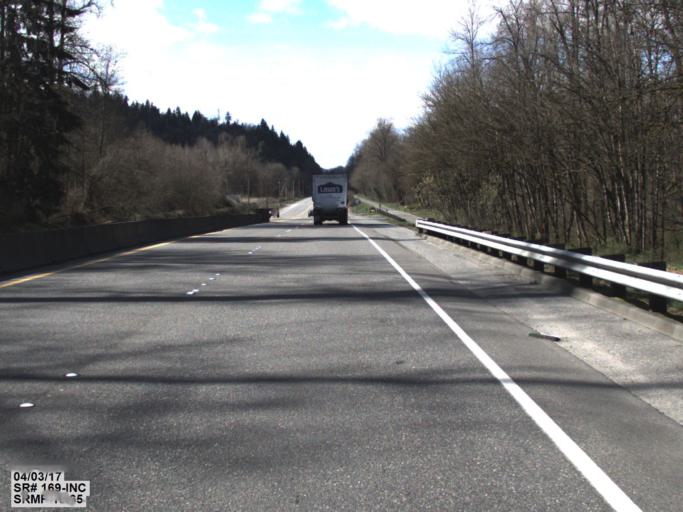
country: US
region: Washington
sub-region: King County
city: Maple Heights-Lake Desire
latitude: 47.4615
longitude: -122.0862
